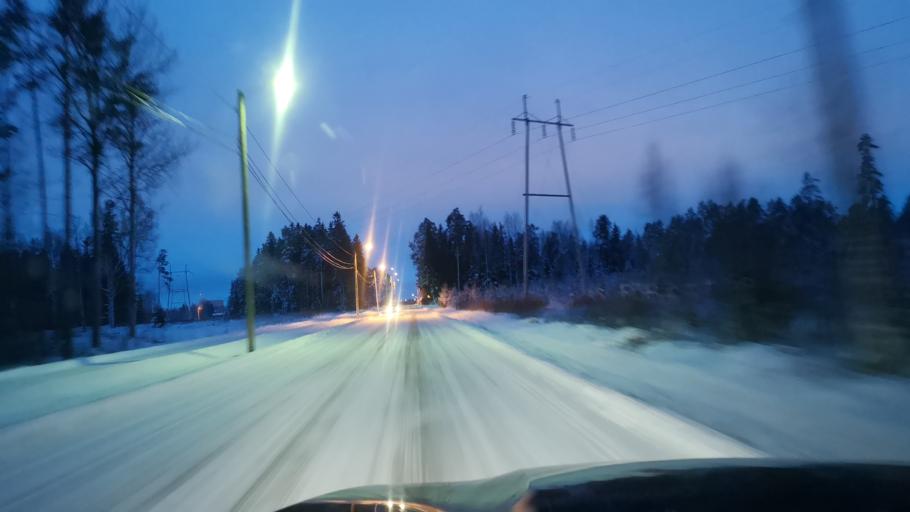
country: FI
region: Varsinais-Suomi
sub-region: Loimaa
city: Loimaa
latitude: 60.8669
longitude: 23.0858
